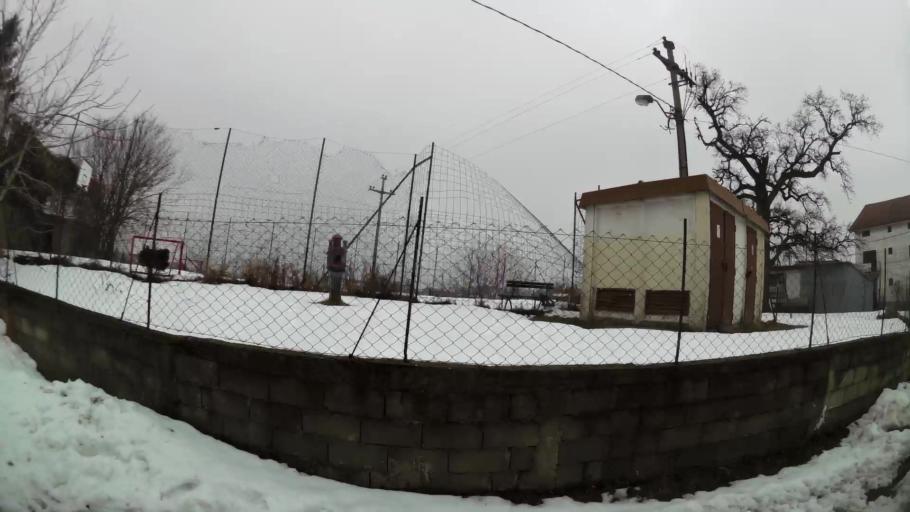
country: RS
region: Central Serbia
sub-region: Belgrade
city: Zvezdara
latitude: 44.7437
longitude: 20.5132
